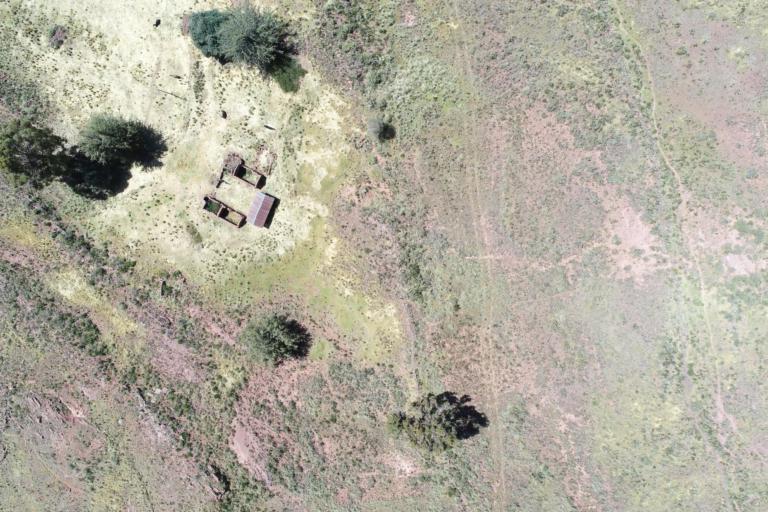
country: BO
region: La Paz
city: Tiahuanaco
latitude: -16.6091
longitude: -68.7642
